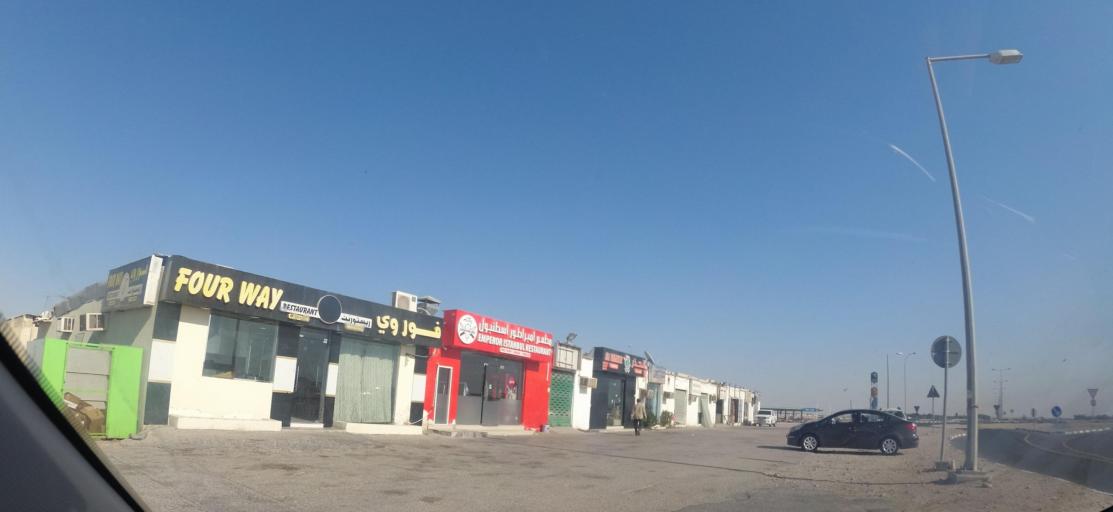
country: QA
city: Al Jumayliyah
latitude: 25.6178
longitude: 51.0840
